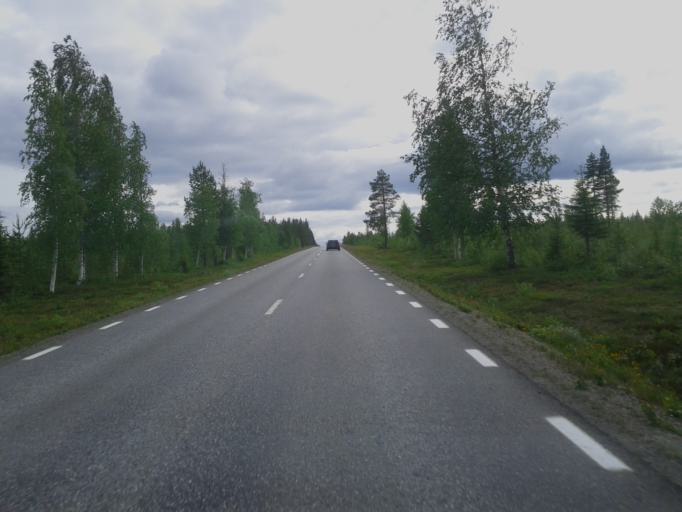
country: SE
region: Vaesterbotten
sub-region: Sorsele Kommun
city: Sorsele
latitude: 65.2305
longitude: 17.6534
